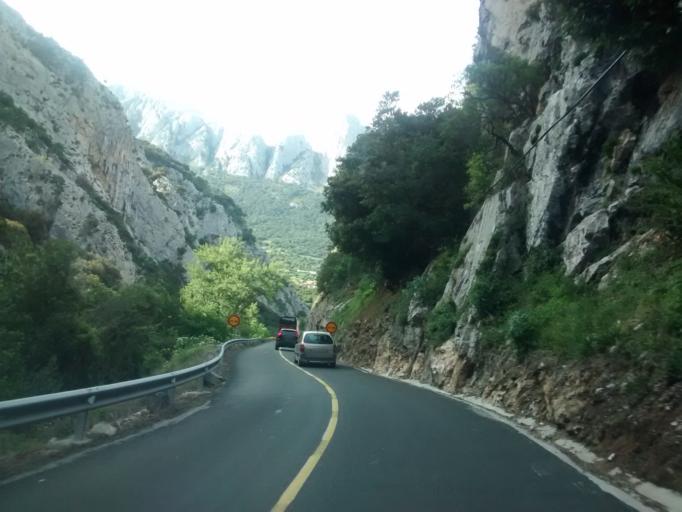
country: ES
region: Cantabria
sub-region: Provincia de Cantabria
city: Potes
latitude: 43.2047
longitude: -4.5936
